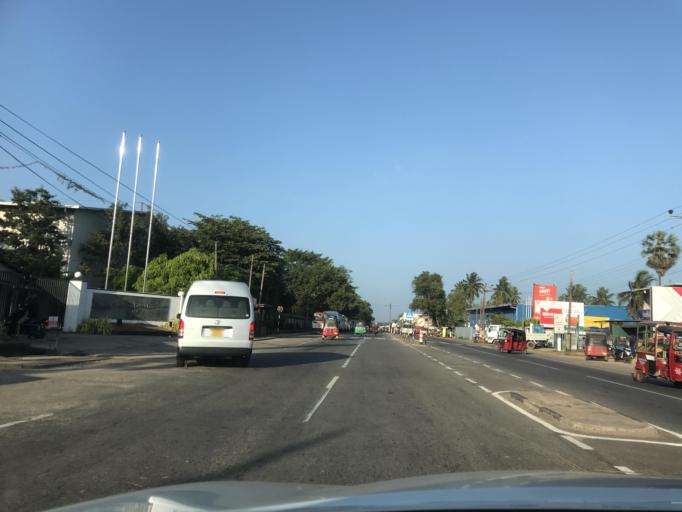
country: LK
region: Western
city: Ja Ela
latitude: 7.0945
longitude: 79.9046
